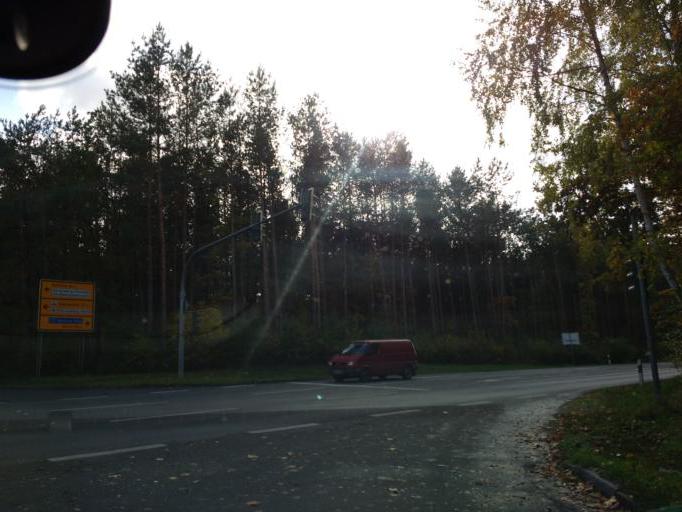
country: DE
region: Brandenburg
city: Strausberg
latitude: 52.5504
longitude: 13.8484
